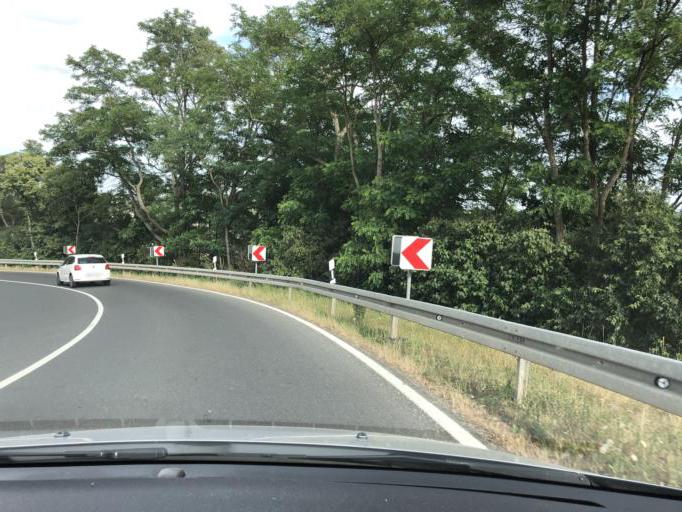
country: DE
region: Thuringia
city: Camburg
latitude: 51.0518
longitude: 11.6921
